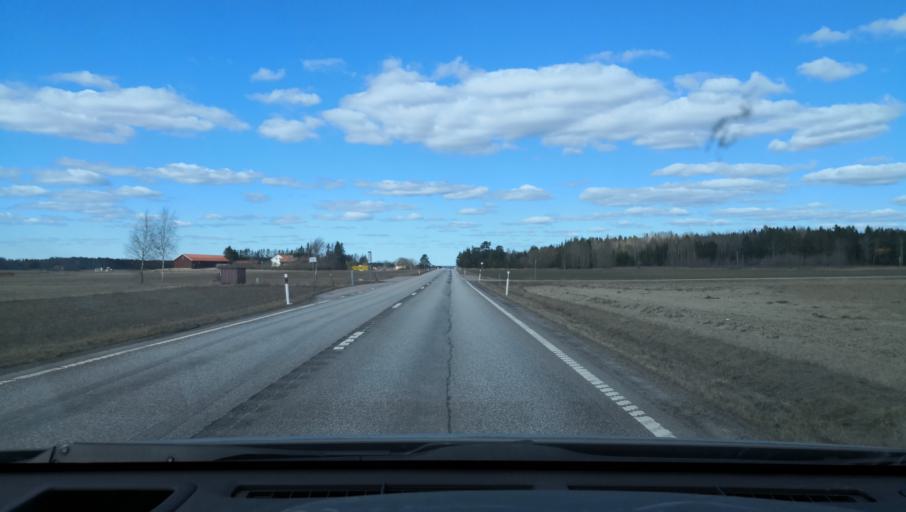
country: SE
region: Vaestmanland
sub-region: Sala Kommun
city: Sala
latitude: 59.8680
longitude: 16.6288
